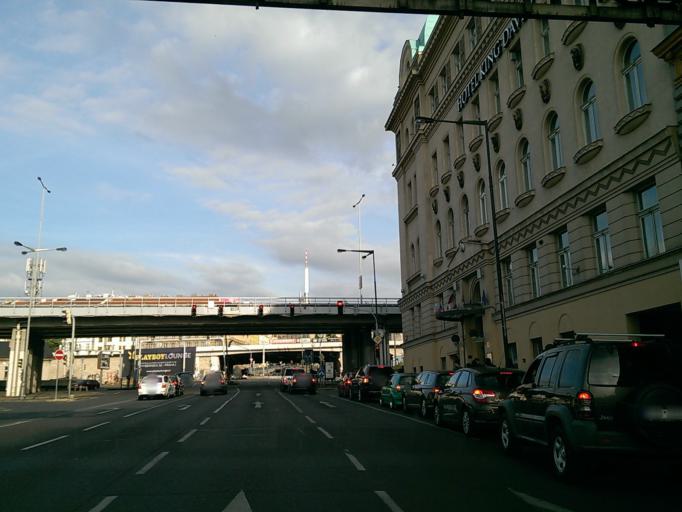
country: CZ
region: Praha
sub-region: Praha 8
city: Karlin
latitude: 50.0868
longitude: 14.4364
